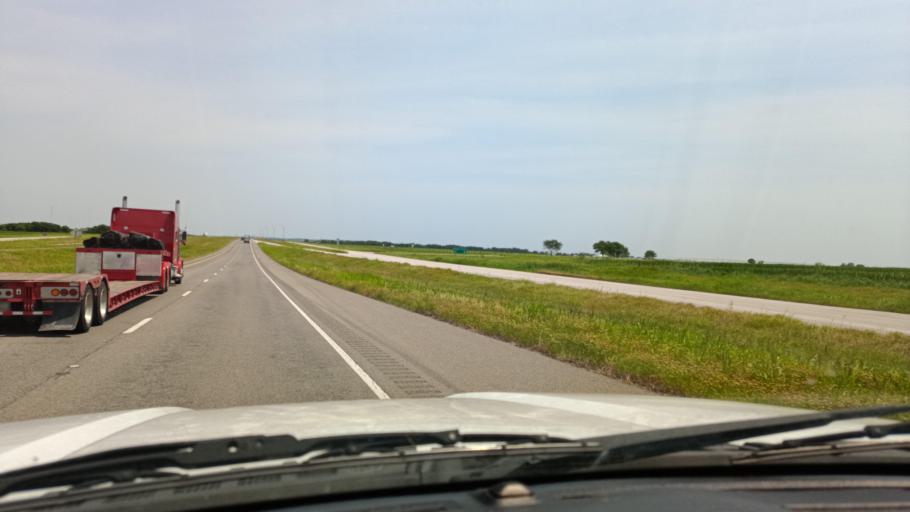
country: US
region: Texas
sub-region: Bell County
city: Little River-Academy
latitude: 31.0218
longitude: -97.3135
